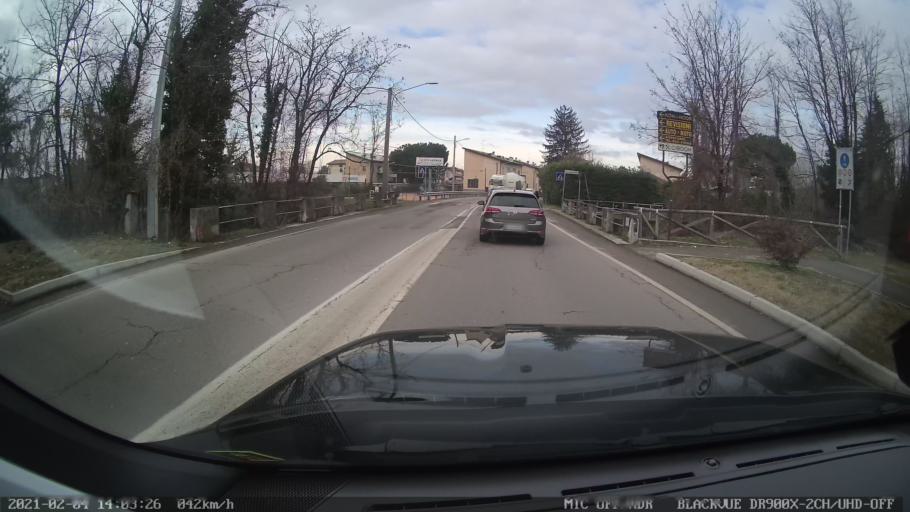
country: IT
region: Lombardy
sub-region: Provincia di Varese
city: Tradate
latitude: 45.7135
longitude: 8.8991
